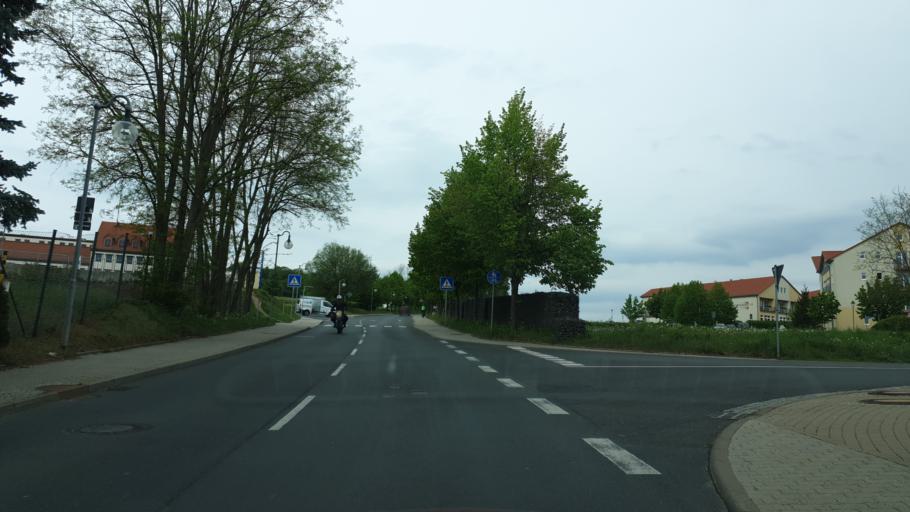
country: DE
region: Saxony
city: Dippoldiswalde
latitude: 50.9059
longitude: 13.6732
